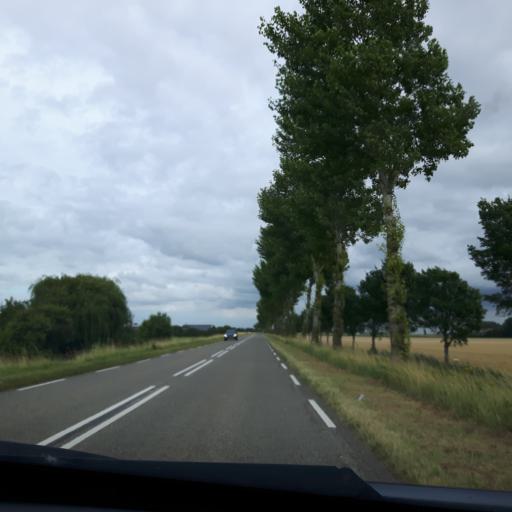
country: NL
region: Zeeland
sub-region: Gemeente Goes
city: Goes
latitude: 51.5616
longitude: 3.8440
